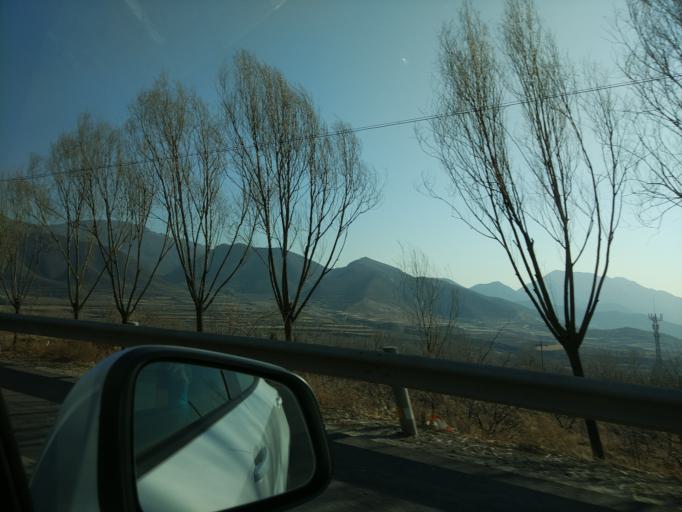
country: CN
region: Hebei
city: Shacheng
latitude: 40.5330
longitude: 115.6270
